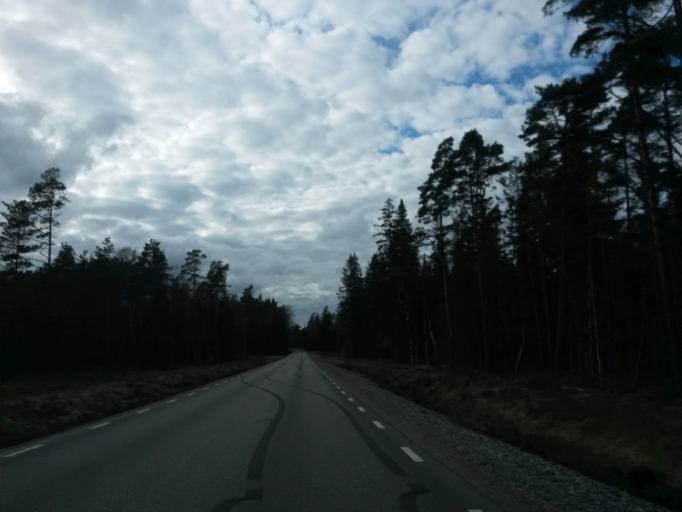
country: SE
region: Vaestra Goetaland
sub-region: Vargarda Kommun
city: Jonstorp
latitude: 57.9448
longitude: 12.6695
